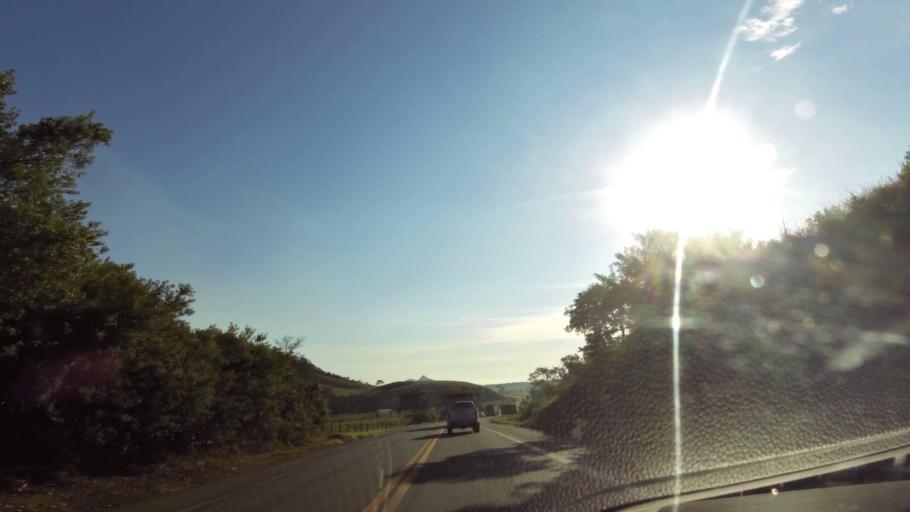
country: BR
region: Espirito Santo
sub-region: Guarapari
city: Guarapari
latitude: -20.6242
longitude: -40.5239
